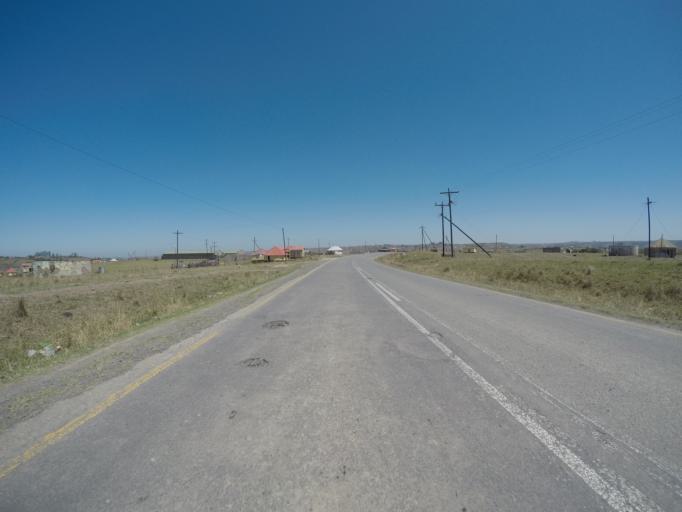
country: ZA
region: Eastern Cape
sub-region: OR Tambo District Municipality
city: Libode
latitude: -31.9115
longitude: 29.0149
